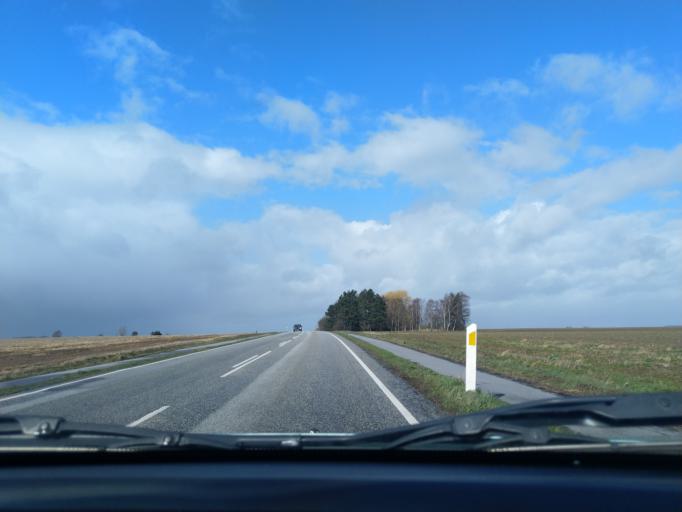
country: DK
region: Zealand
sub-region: Naestved Kommune
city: Naestved
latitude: 55.3087
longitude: 11.6868
